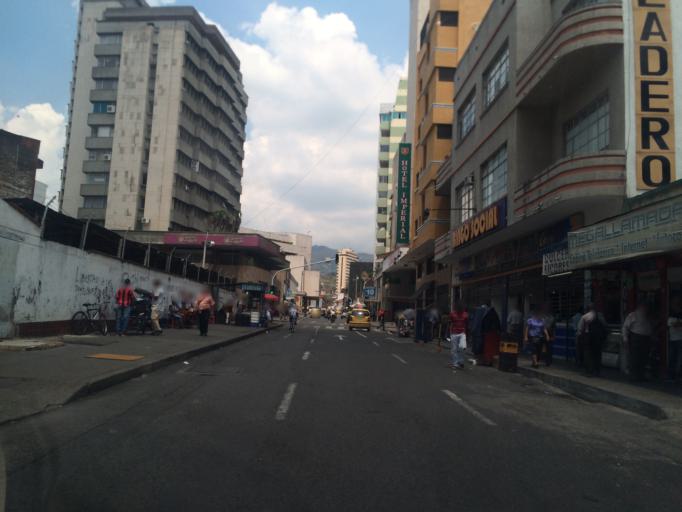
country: CO
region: Valle del Cauca
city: Cali
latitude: 3.4515
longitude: -76.5340
